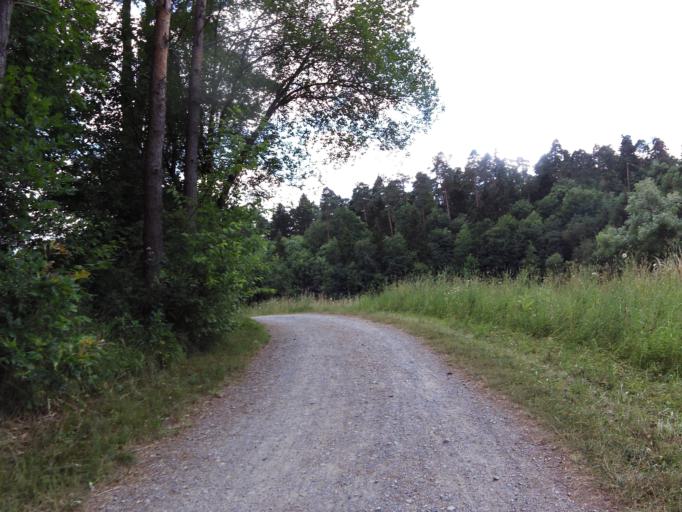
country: DE
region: Bavaria
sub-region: Regierungsbezirk Unterfranken
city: Gadheim
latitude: 49.8359
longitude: 9.9171
